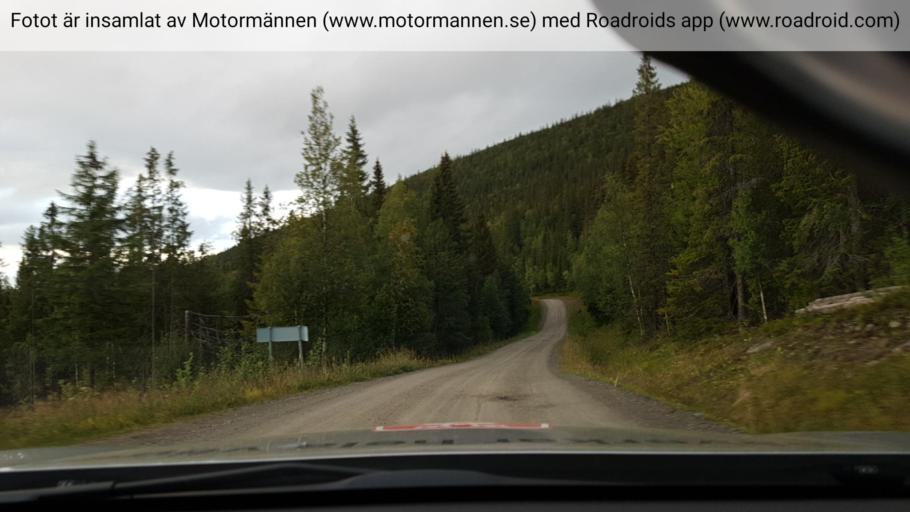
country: SE
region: Vaesterbotten
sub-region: Vilhelmina Kommun
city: Sjoberg
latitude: 65.6090
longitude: 15.2661
